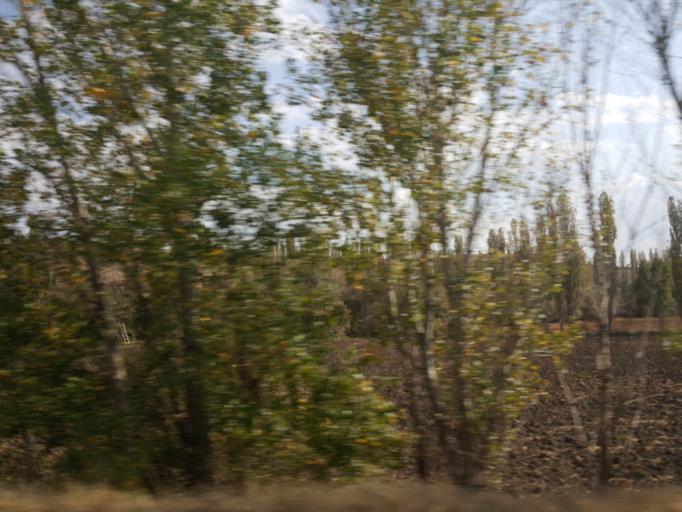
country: TR
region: Corum
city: Sungurlu
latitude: 40.1881
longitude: 34.4977
